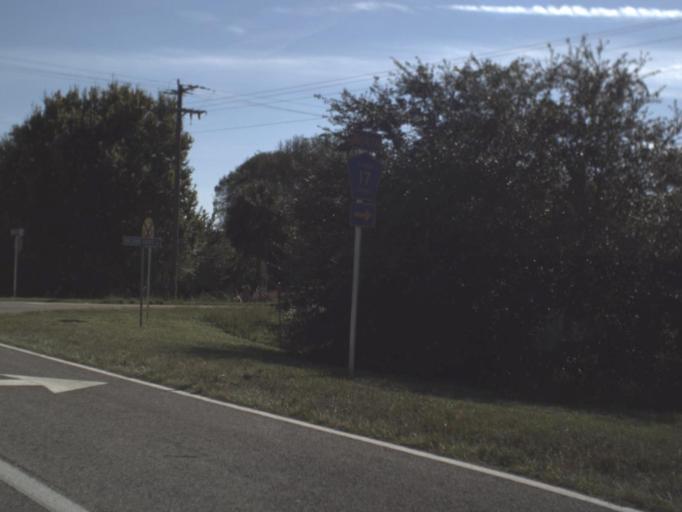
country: US
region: Florida
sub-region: Highlands County
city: Placid Lakes
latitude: 27.0276
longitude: -81.3415
